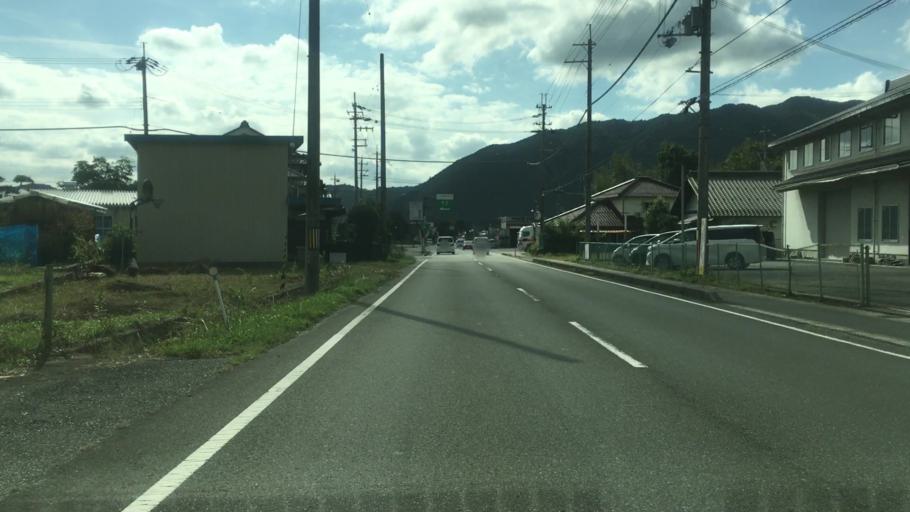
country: JP
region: Kyoto
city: Fukuchiyama
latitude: 35.2445
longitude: 135.0075
